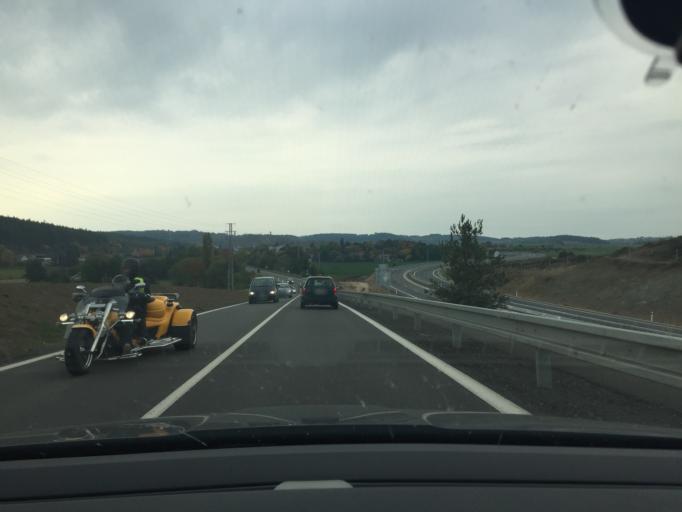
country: CZ
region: Central Bohemia
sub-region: Okres Pribram
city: Pribram
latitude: 49.7032
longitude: 14.0872
